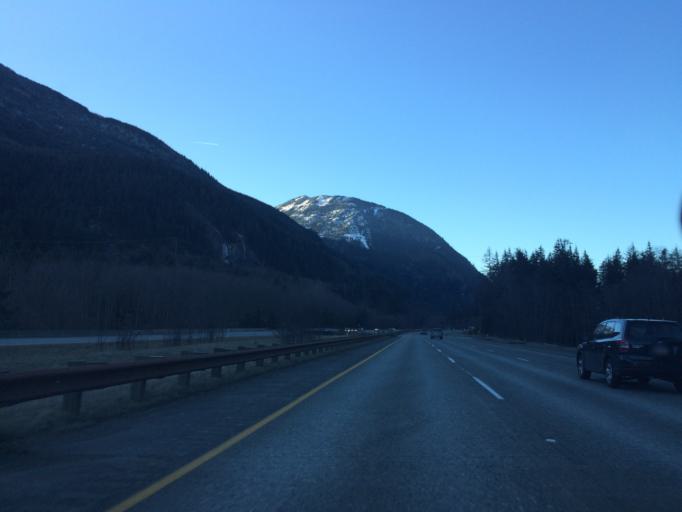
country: US
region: Washington
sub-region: King County
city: Tanner
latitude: 47.4292
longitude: -121.6273
